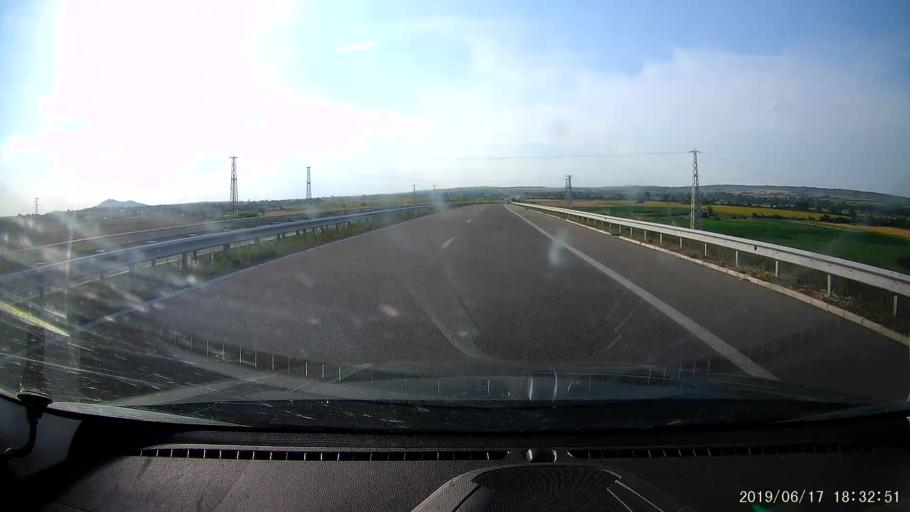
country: BG
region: Khaskovo
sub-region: Obshtina Dimitrovgrad
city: Dimitrovgrad
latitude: 42.0675
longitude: 25.4697
